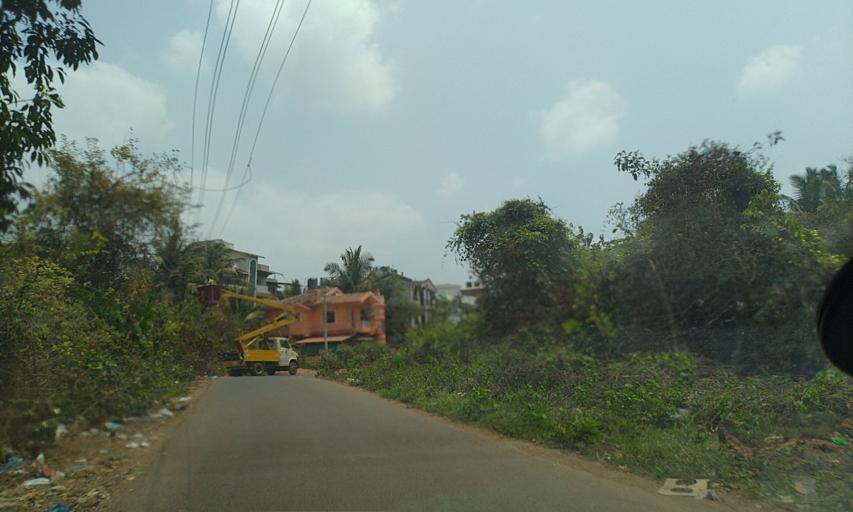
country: IN
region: Goa
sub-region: North Goa
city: Panaji
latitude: 15.5230
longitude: 73.8254
